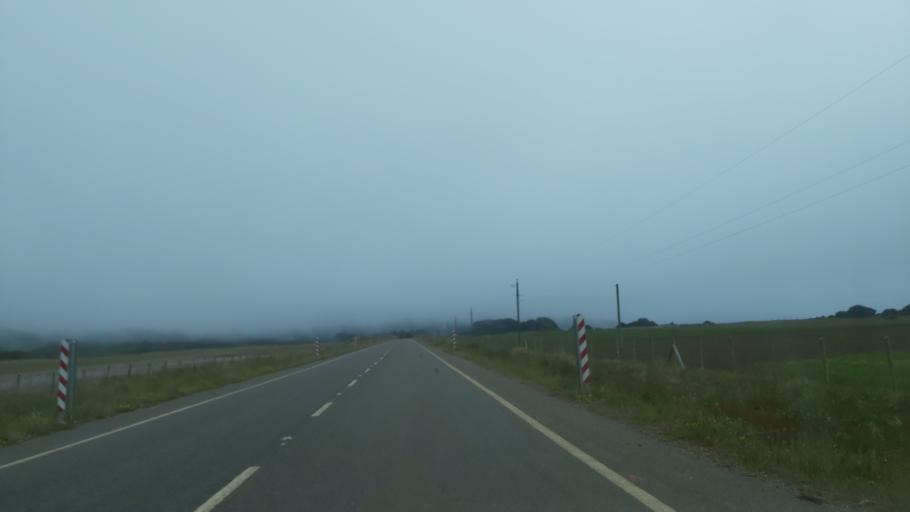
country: CL
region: Maule
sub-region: Provincia de Cauquenes
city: Cauquenes
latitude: -35.9962
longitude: -72.7712
